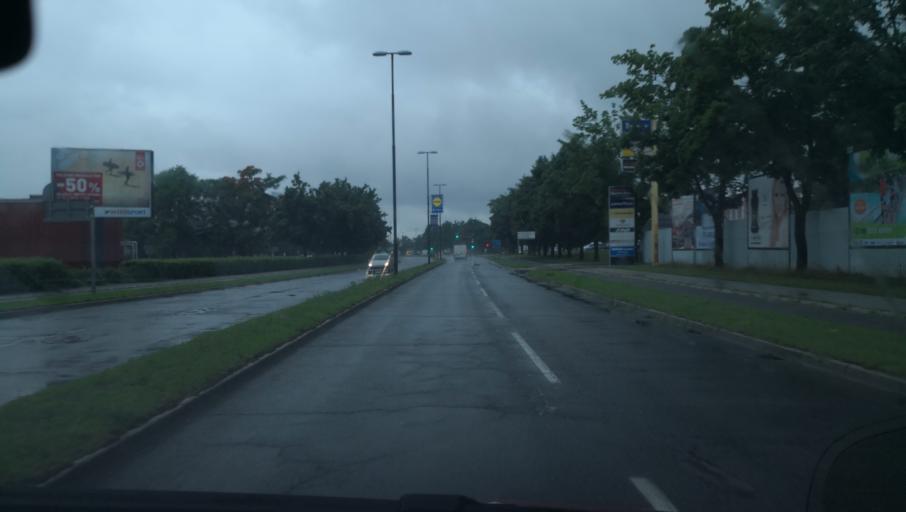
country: SI
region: Dol pri Ljubljani
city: Dol pri Ljubljani
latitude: 46.0553
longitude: 14.5642
